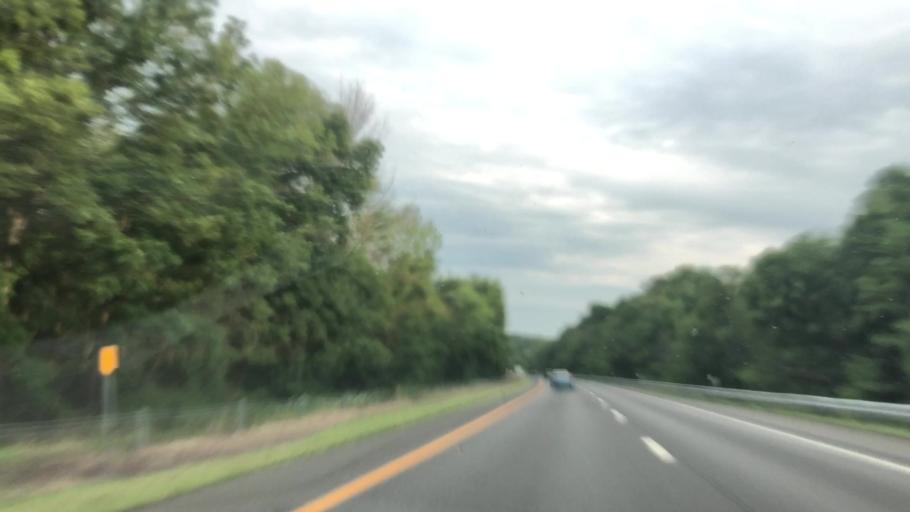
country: US
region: New York
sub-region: Ulster County
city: Tillson
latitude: 41.7960
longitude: -74.0522
